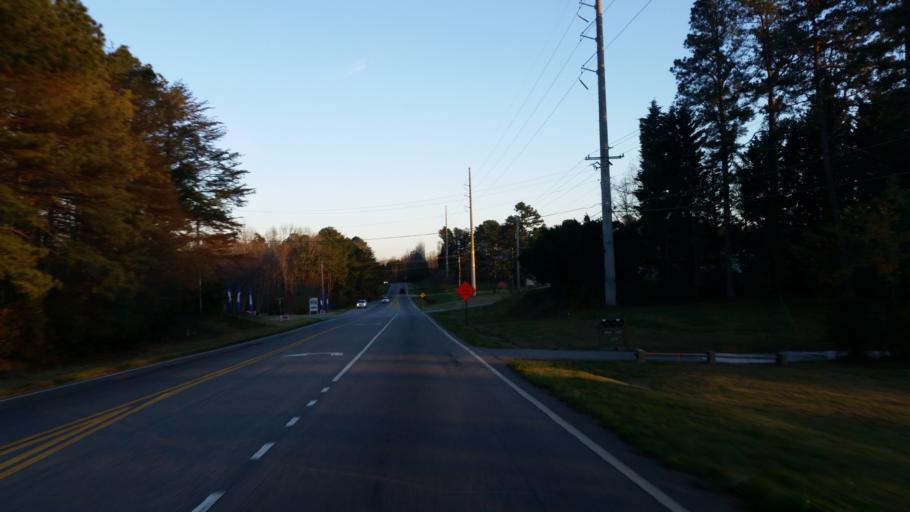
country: US
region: Georgia
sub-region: Hall County
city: Oakwood
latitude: 34.3173
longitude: -84.0012
